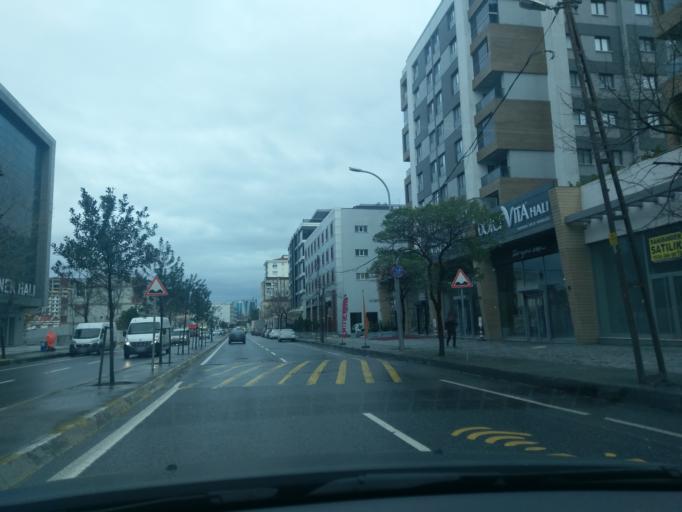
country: TR
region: Istanbul
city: Mahmutbey
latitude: 41.0499
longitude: 28.8302
